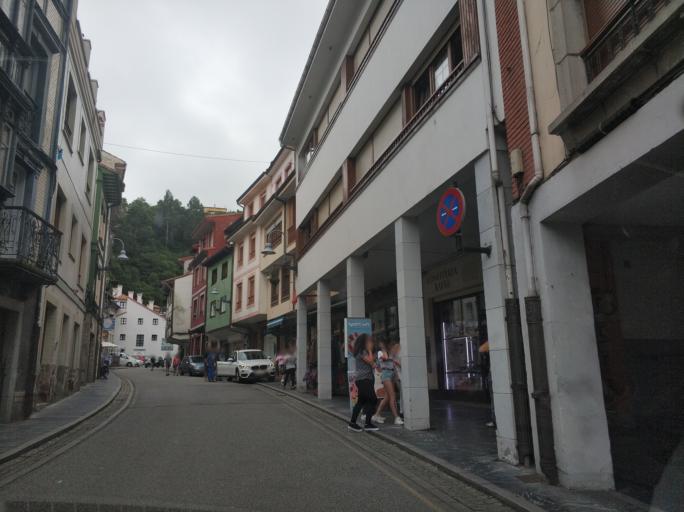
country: ES
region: Asturias
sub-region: Province of Asturias
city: Cudillero
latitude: 43.5627
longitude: -6.1465
